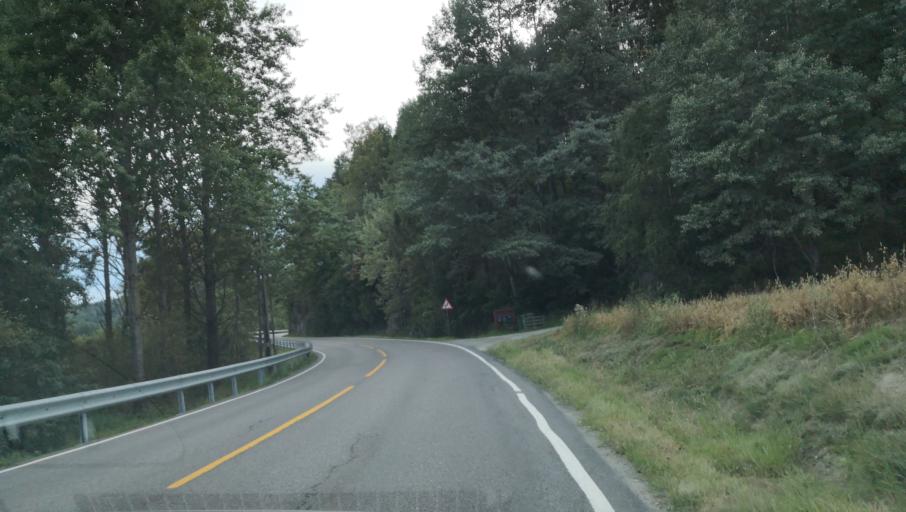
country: NO
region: Ostfold
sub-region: Hobol
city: Tomter
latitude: 59.7005
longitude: 11.0467
